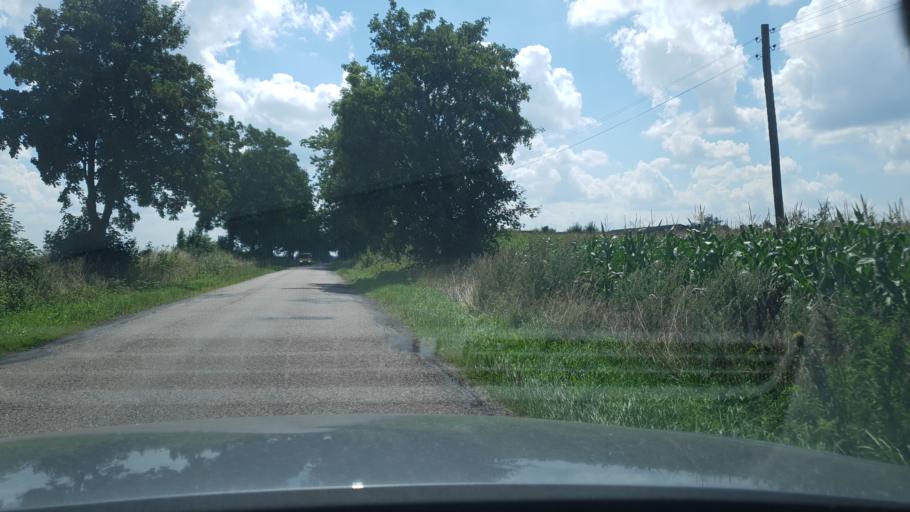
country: PL
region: Kujawsko-Pomorskie
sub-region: Powiat wabrzeski
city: Pluznica
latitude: 53.2866
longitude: 18.8314
